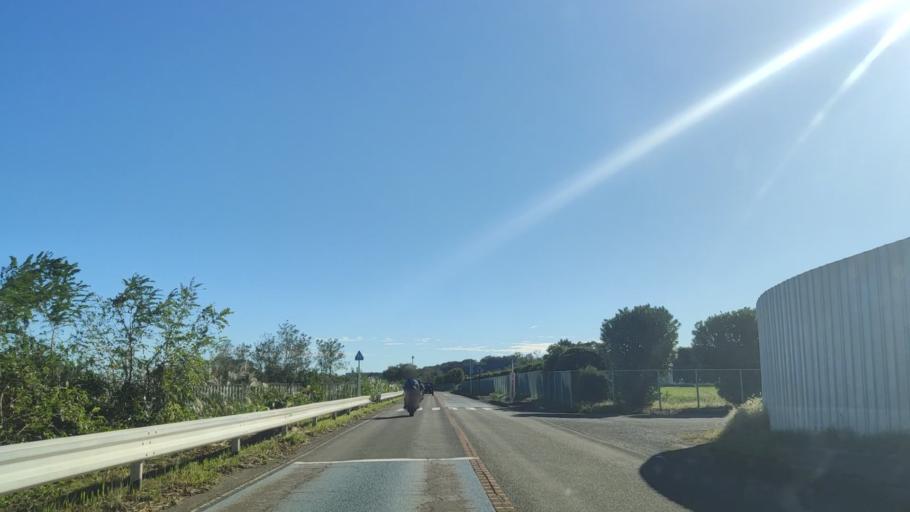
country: JP
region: Kanagawa
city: Zama
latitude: 35.5031
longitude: 139.3725
